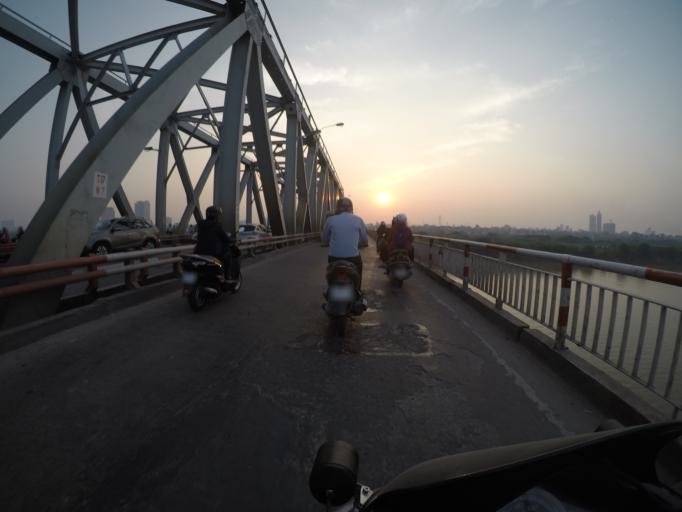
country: VN
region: Ha Noi
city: Hoan Kiem
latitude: 21.0388
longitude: 105.8621
